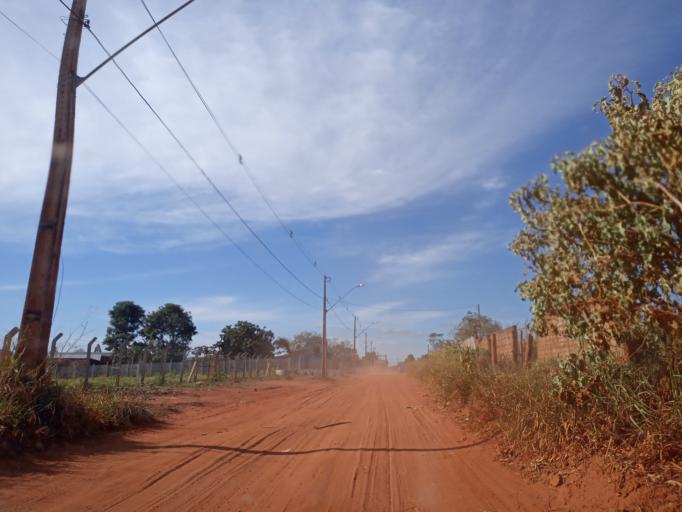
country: BR
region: Minas Gerais
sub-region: Ituiutaba
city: Ituiutaba
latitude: -18.9584
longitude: -49.4900
